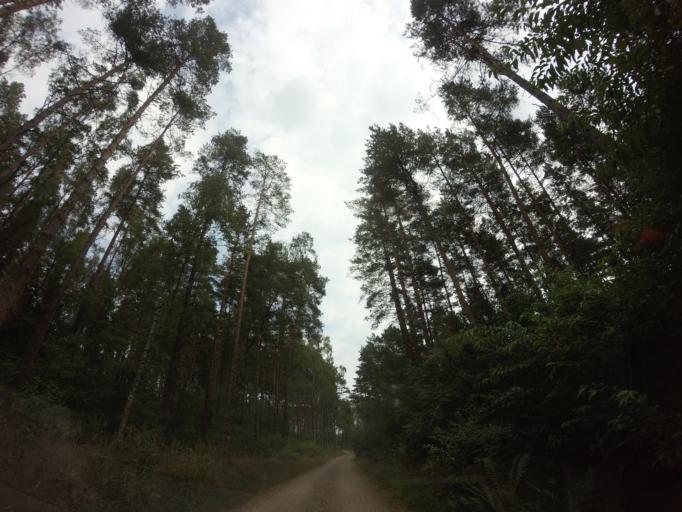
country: PL
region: West Pomeranian Voivodeship
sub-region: Powiat drawski
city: Drawsko Pomorskie
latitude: 53.4591
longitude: 15.7339
